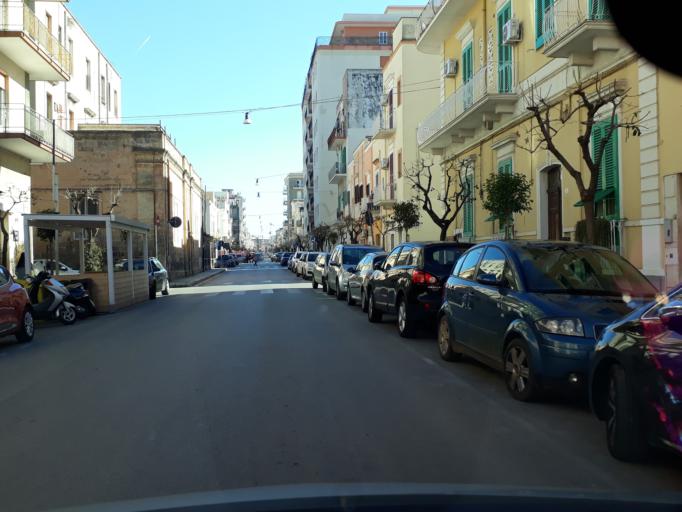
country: IT
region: Apulia
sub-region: Provincia di Bari
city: Monopoli
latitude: 40.9543
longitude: 17.2977
